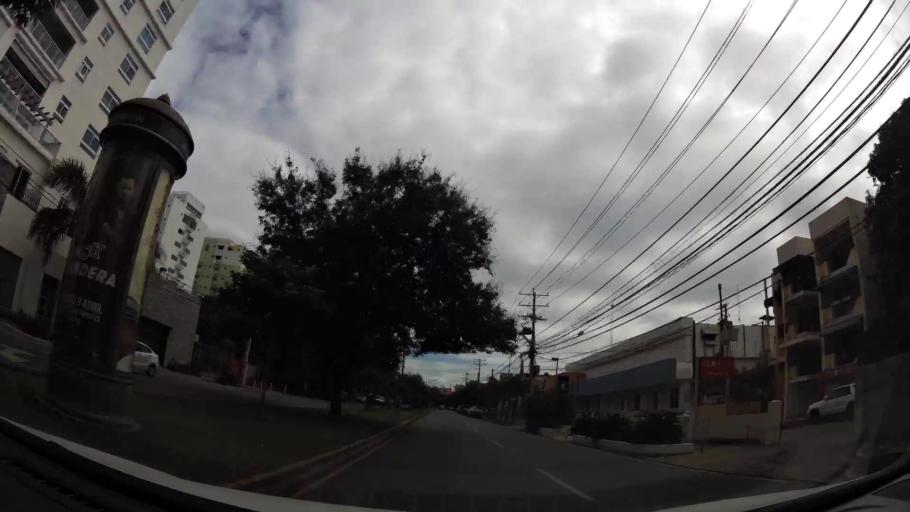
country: DO
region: Nacional
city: Bella Vista
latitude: 18.4512
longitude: -69.9469
